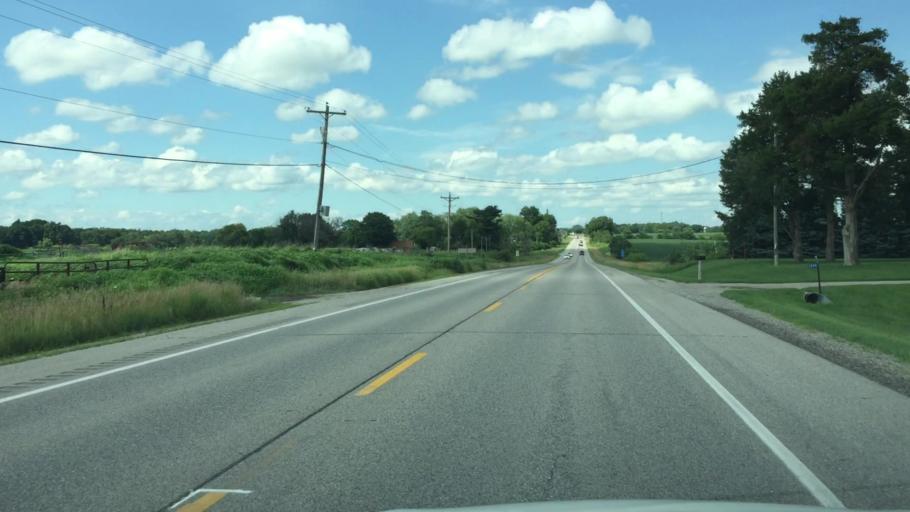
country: US
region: Iowa
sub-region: Johnson County
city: Iowa City
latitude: 41.7223
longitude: -91.4786
